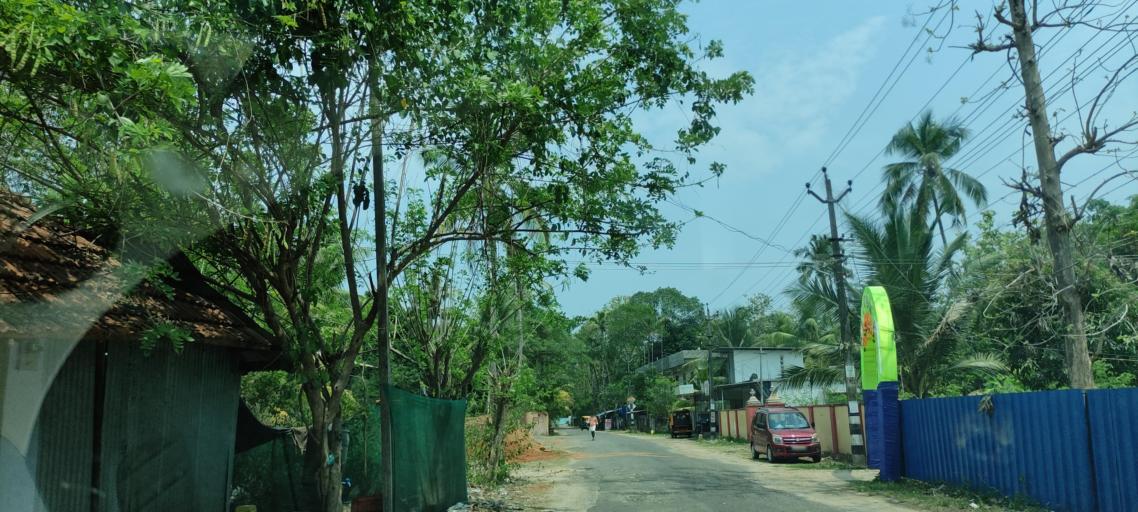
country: IN
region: Kerala
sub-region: Alappuzha
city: Vayalar
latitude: 9.7224
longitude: 76.3387
